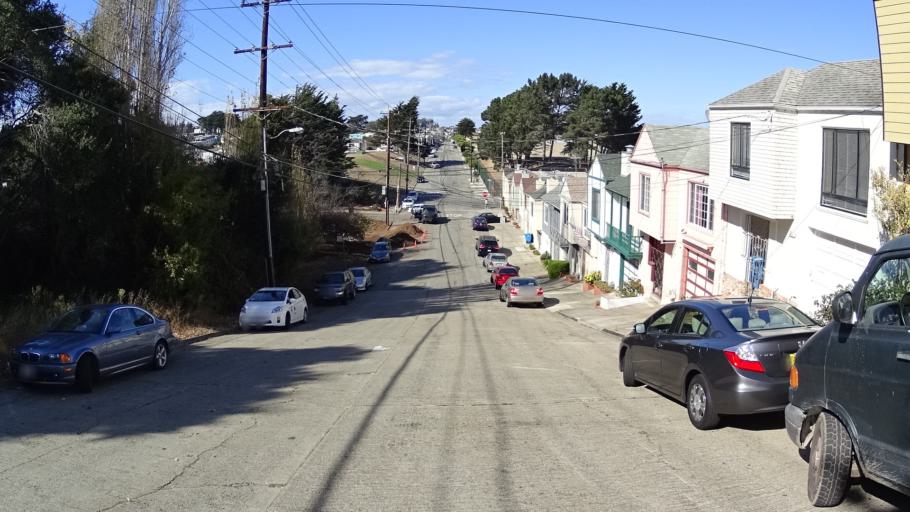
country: US
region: California
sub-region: San Mateo County
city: Brisbane
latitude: 37.7219
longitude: -122.4121
